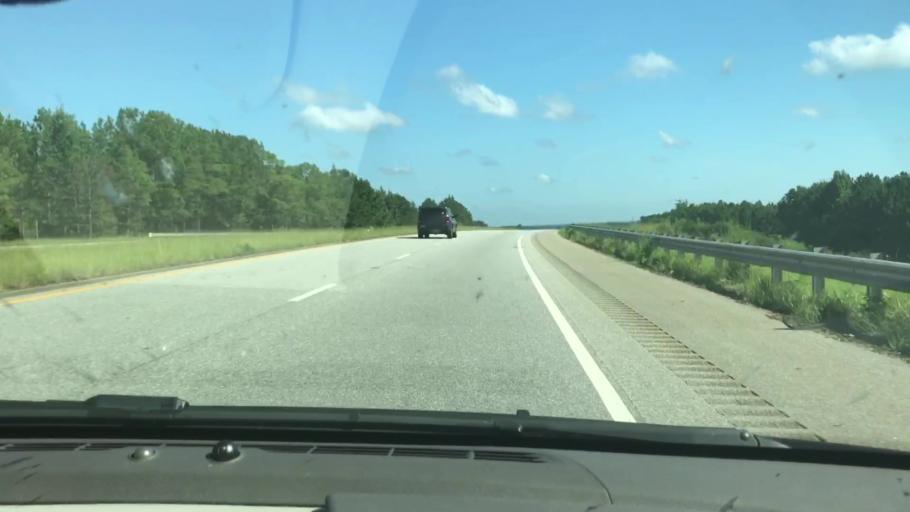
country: US
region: Alabama
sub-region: Barbour County
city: Eufaula
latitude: 32.1590
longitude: -85.1781
